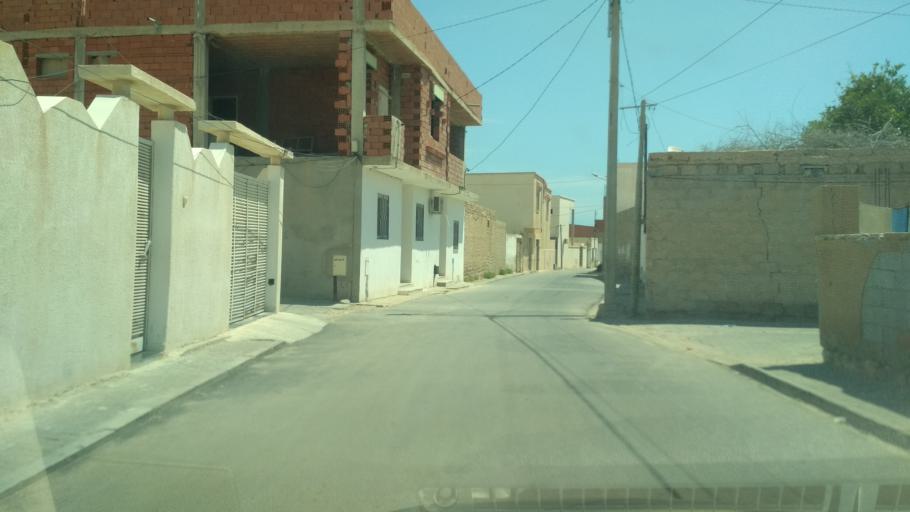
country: TN
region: Qabis
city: Gabes
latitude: 33.9400
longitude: 10.0672
